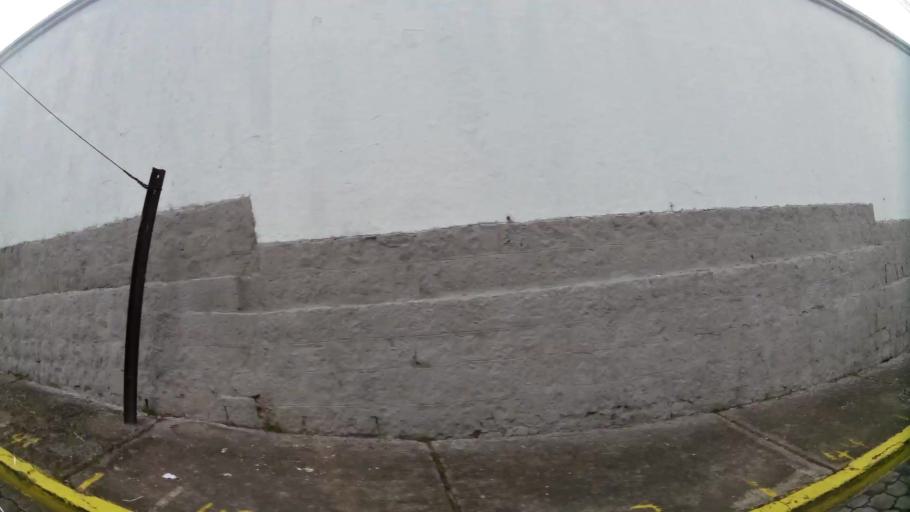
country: EC
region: Pichincha
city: Sangolqui
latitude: -0.3378
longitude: -78.4529
